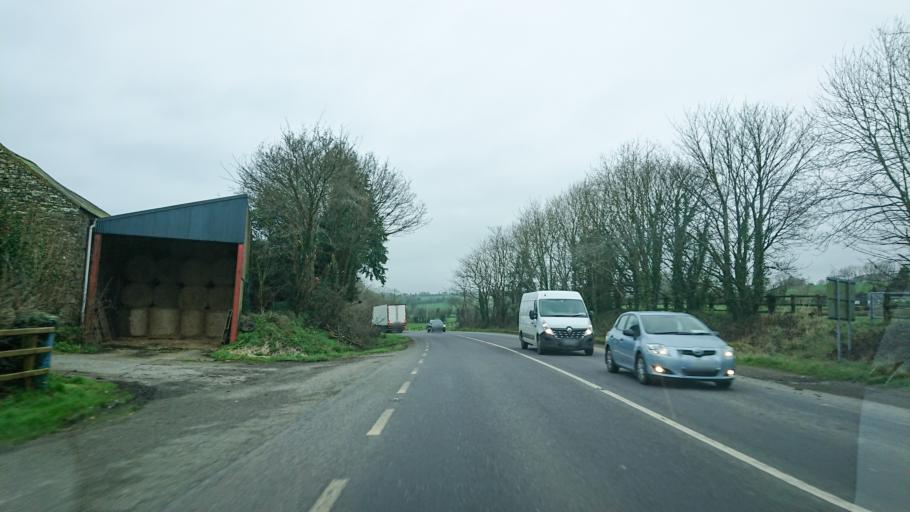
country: IE
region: Munster
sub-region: County Cork
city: Bandon
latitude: 51.7437
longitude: -8.8172
